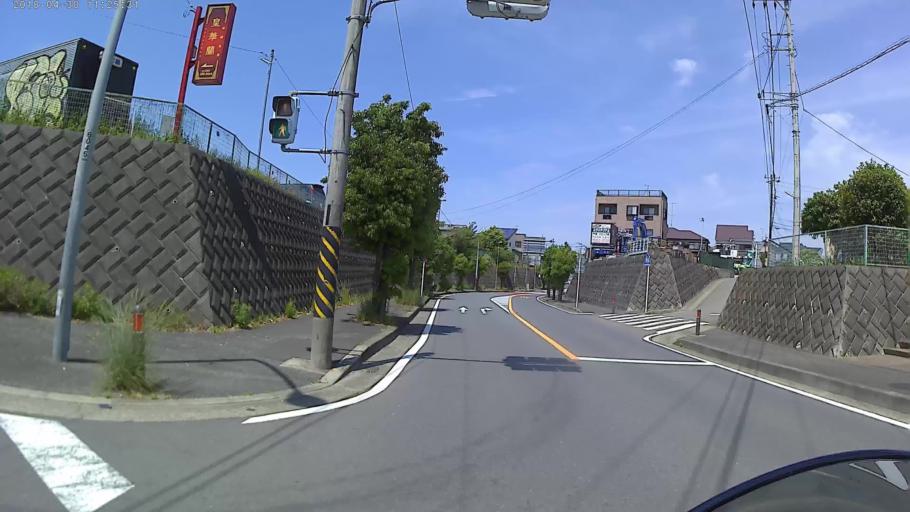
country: JP
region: Kanagawa
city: Zama
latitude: 35.4775
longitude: 139.4140
